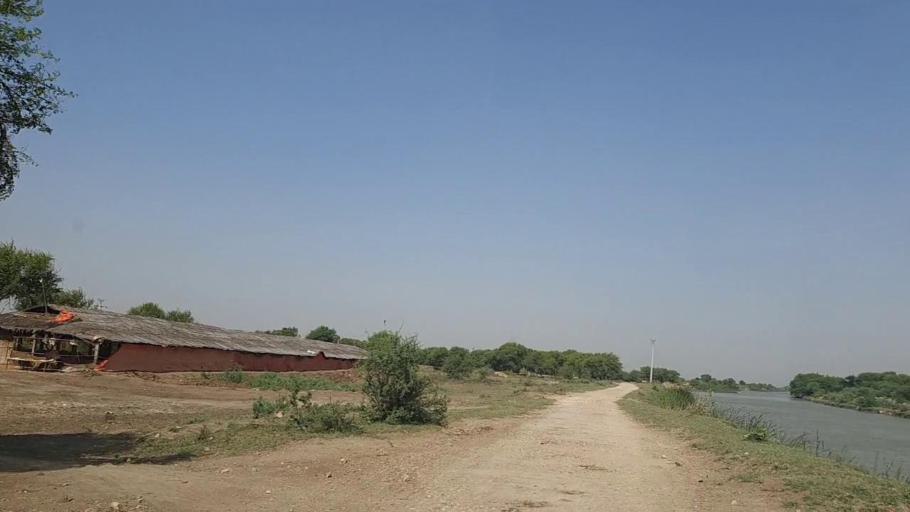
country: PK
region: Sindh
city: Daro Mehar
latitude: 24.7363
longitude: 68.1551
